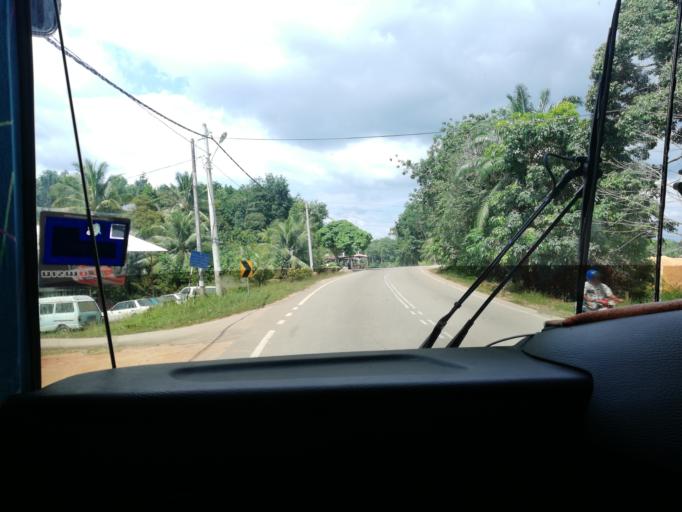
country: MY
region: Perak
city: Parit Buntar
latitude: 5.1255
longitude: 100.5683
